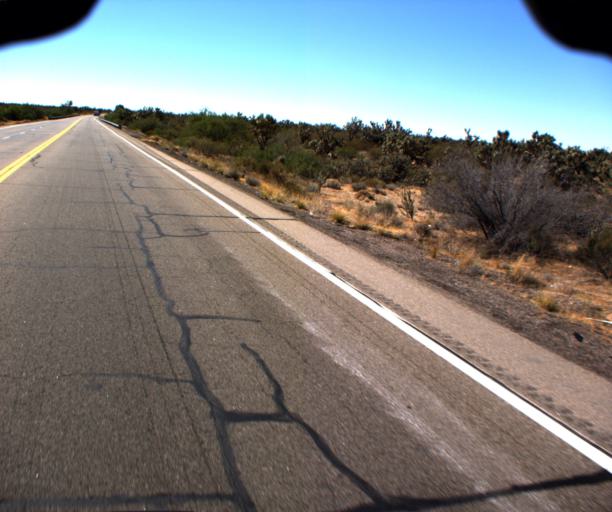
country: US
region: Arizona
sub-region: Yavapai County
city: Congress
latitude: 34.2741
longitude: -113.0972
